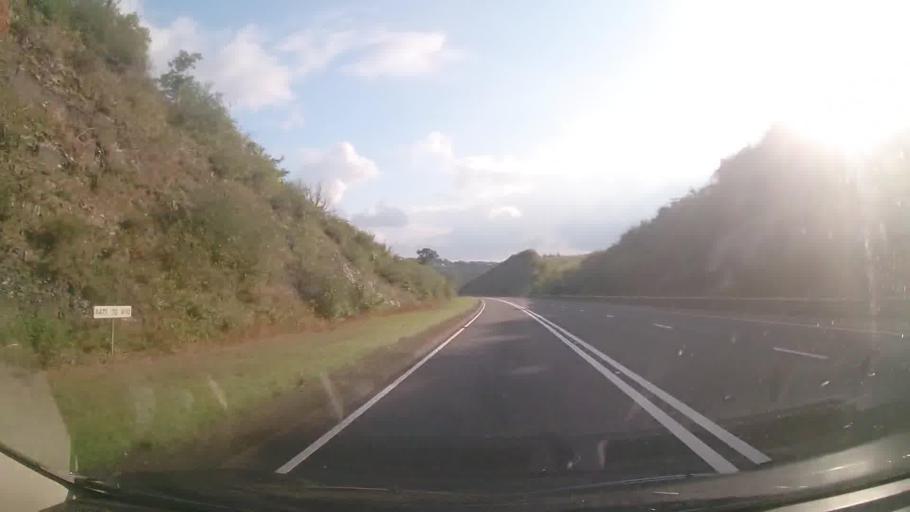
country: GB
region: Wales
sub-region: Pembrokeshire
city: Kilgetty
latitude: 51.7423
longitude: -4.7007
